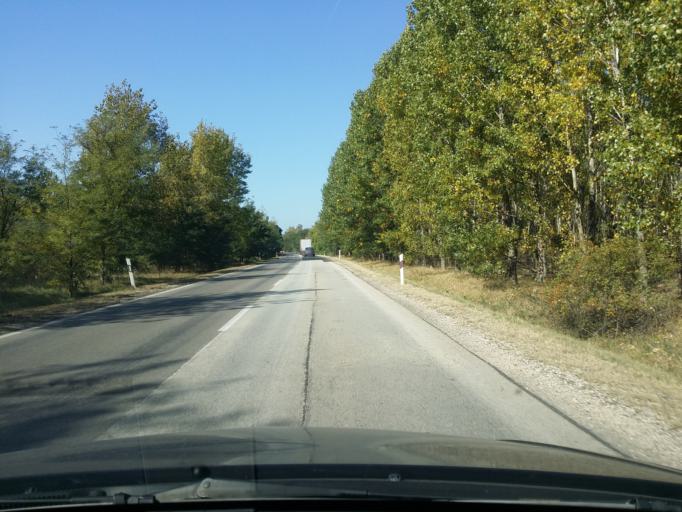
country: HU
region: Bacs-Kiskun
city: Nyarlorinc
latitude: 46.8878
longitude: 19.8361
